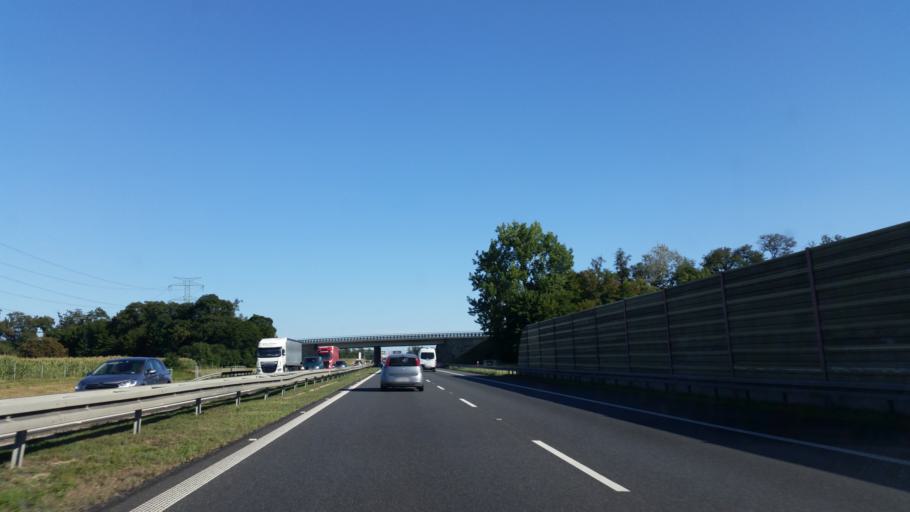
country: PL
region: Lower Silesian Voivodeship
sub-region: Powiat olawski
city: Wierzbno
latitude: 50.8905
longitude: 17.1871
